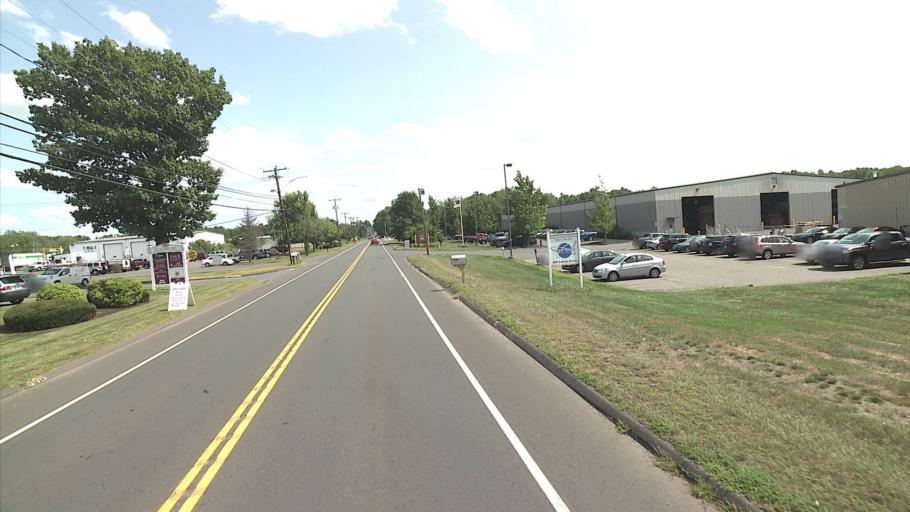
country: US
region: Connecticut
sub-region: Hartford County
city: South Windsor
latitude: 41.8519
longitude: -72.5818
